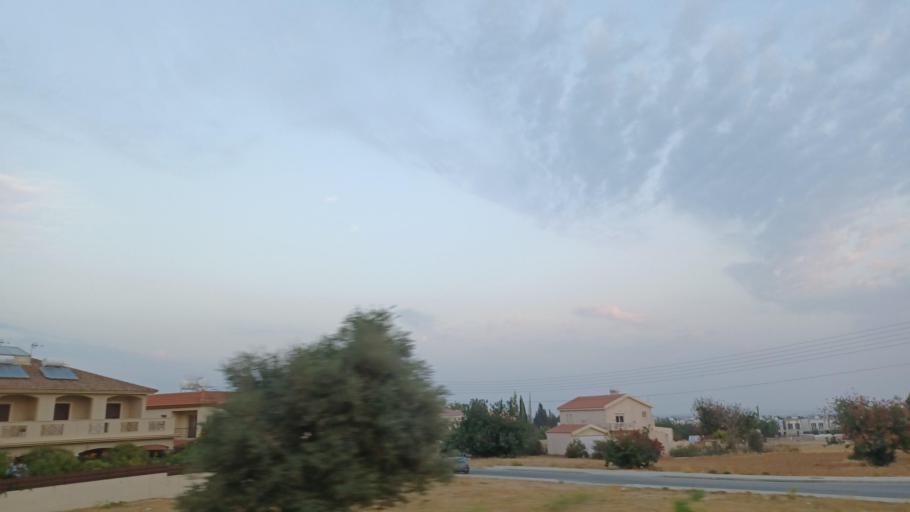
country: CY
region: Limassol
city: Ypsonas
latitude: 34.6968
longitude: 32.9668
